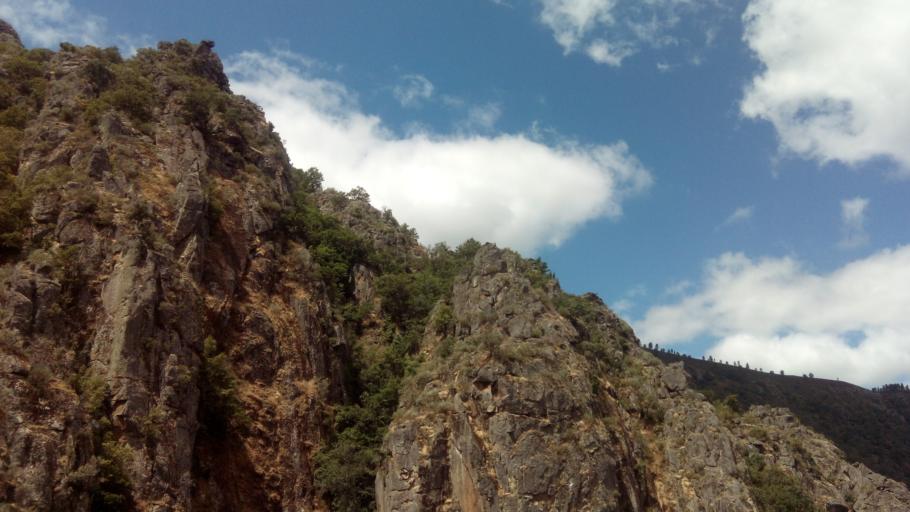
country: ES
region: Galicia
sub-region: Provincia de Lugo
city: Sober
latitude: 42.3903
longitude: -7.6217
